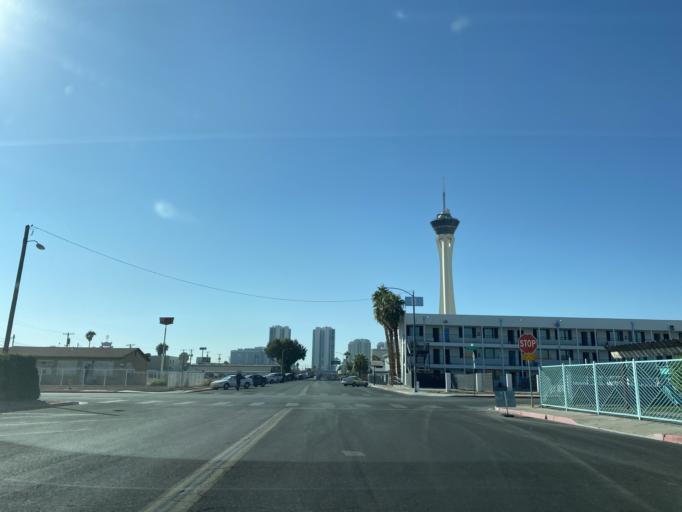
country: US
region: Nevada
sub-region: Clark County
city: Las Vegas
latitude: 36.1551
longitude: -115.1526
